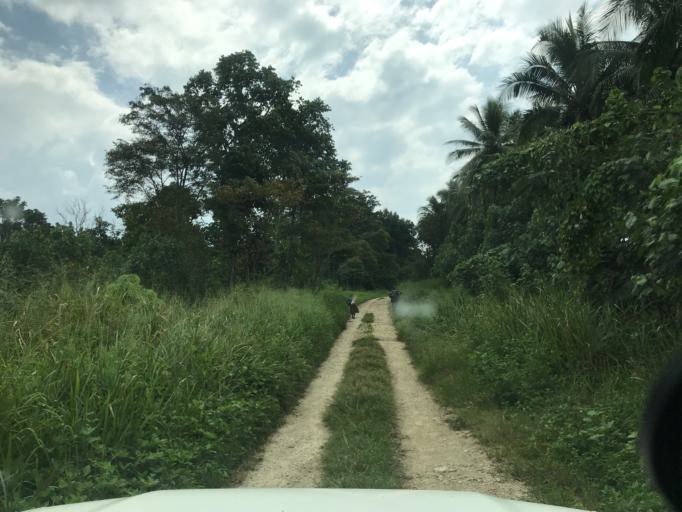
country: VU
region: Sanma
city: Port-Olry
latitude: -15.1736
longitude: 166.9522
